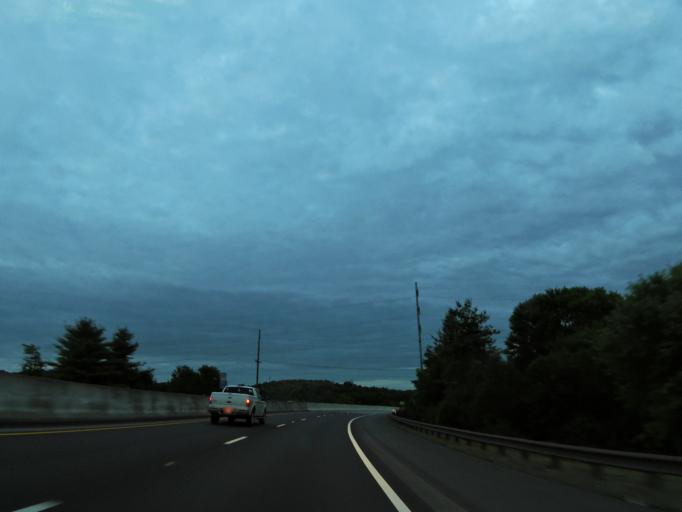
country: US
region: Tennessee
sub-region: Davidson County
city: Nashville
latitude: 36.2321
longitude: -86.8265
